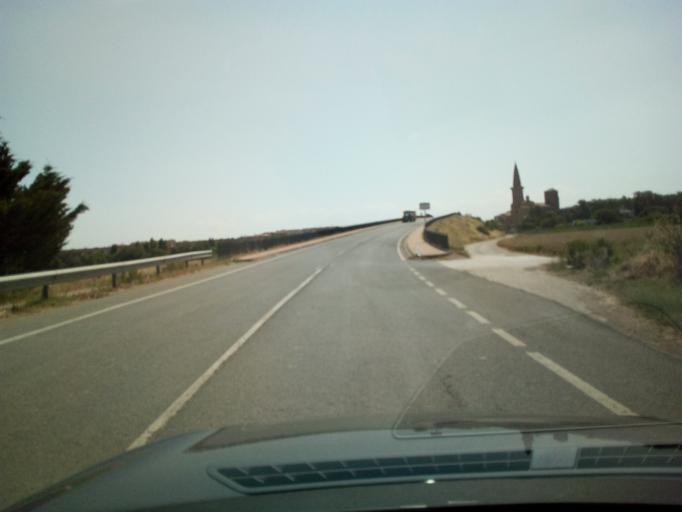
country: ES
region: Navarre
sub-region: Provincia de Navarra
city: Olite
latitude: 42.4816
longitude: -1.6430
